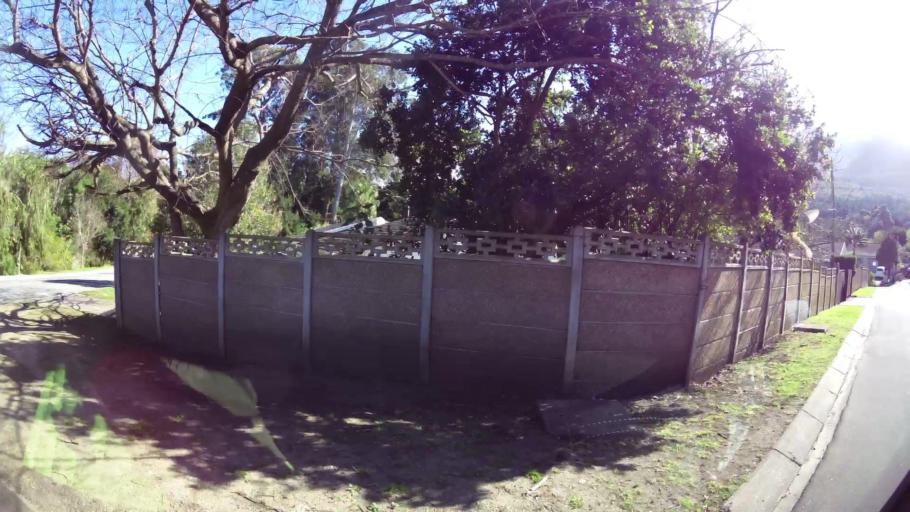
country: ZA
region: Western Cape
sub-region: Eden District Municipality
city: George
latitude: -33.9425
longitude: 22.4702
